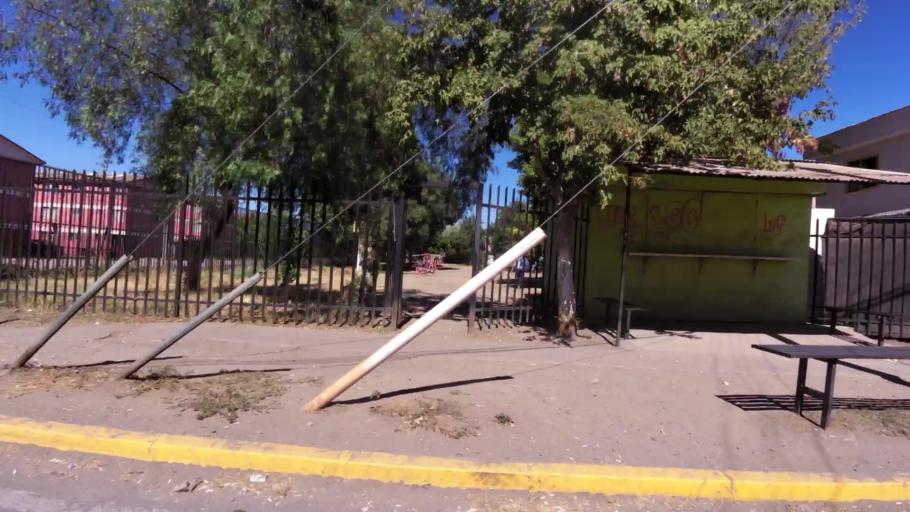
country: CL
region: O'Higgins
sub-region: Provincia de Colchagua
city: Chimbarongo
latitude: -34.5929
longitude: -70.9998
